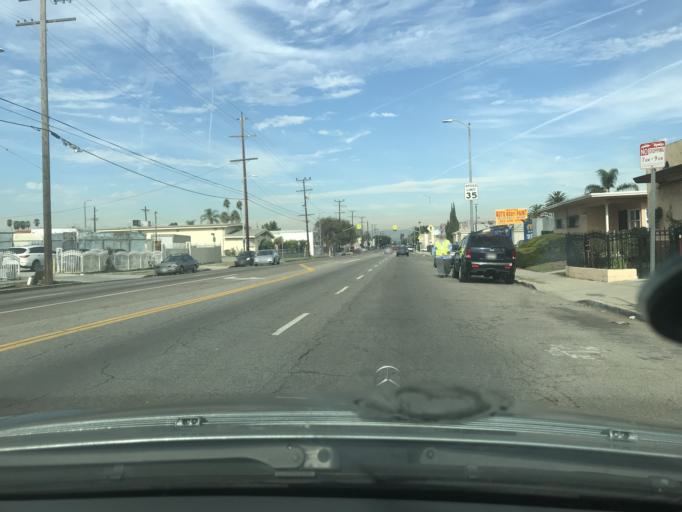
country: US
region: California
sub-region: Los Angeles County
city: Westmont
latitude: 33.9385
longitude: -118.2826
